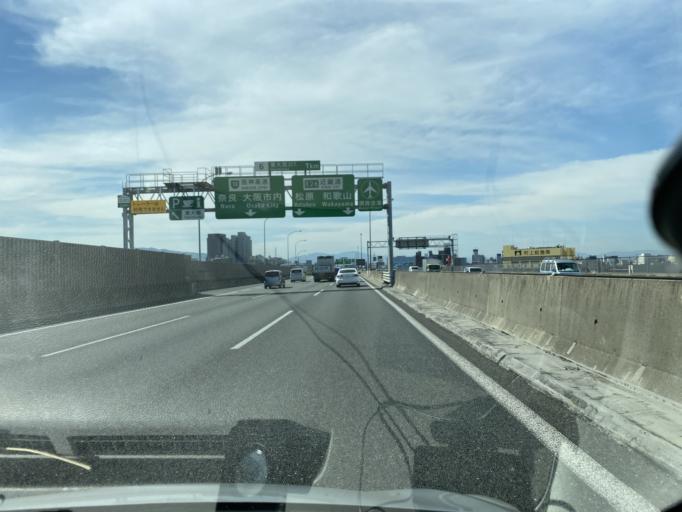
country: JP
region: Osaka
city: Daitocho
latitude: 34.6893
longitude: 135.5939
